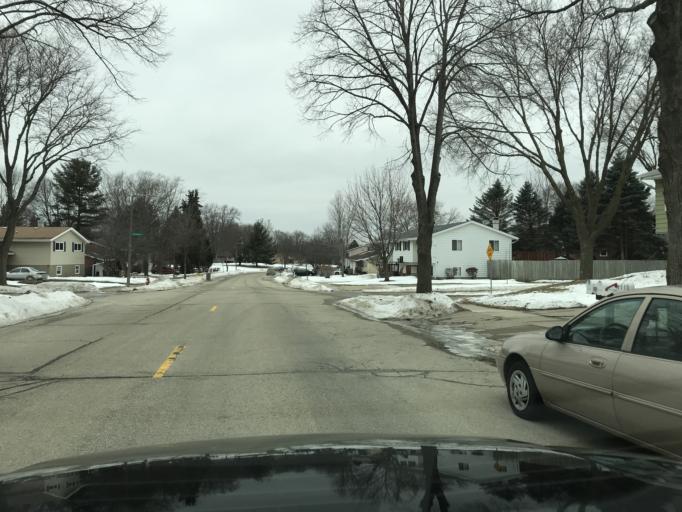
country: US
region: Wisconsin
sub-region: Dane County
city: Monona
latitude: 43.0822
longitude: -89.2849
